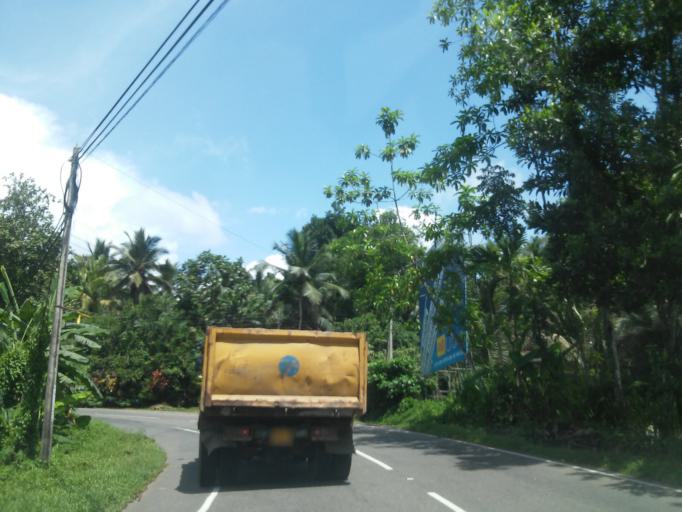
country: LK
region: Sabaragamuwa
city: Ratnapura
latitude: 6.7268
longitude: 80.3300
